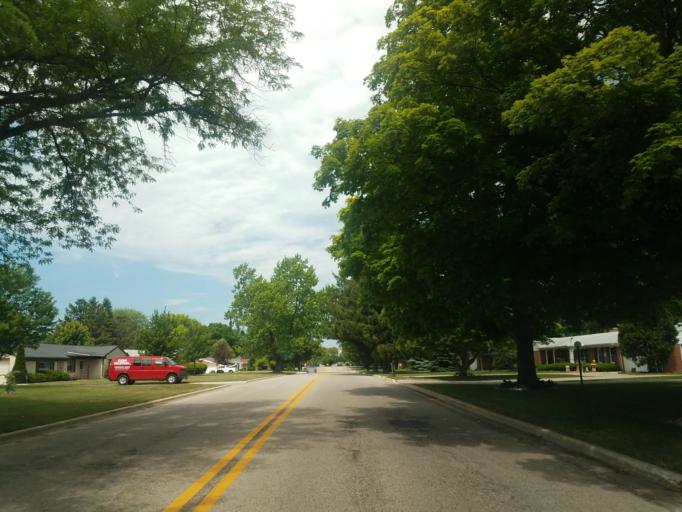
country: US
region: Illinois
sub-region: McLean County
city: Bloomington
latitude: 40.4919
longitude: -88.9622
